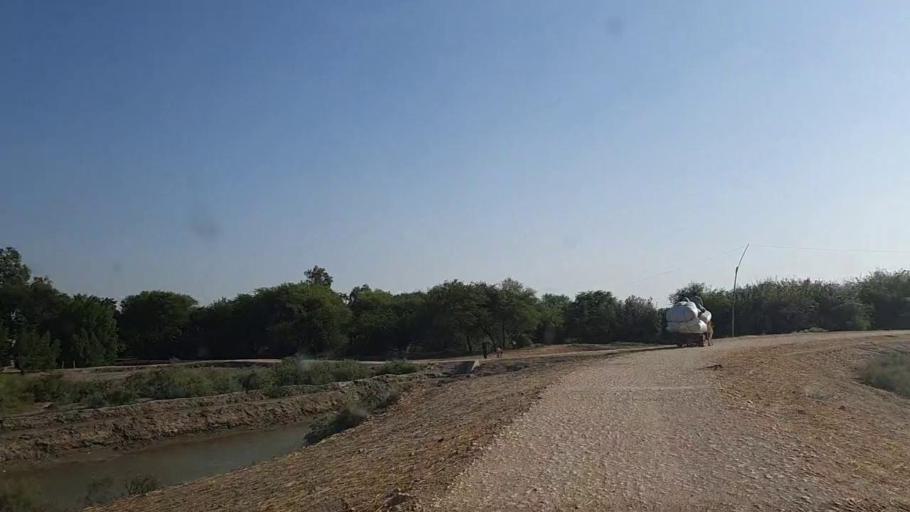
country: PK
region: Sindh
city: Daro Mehar
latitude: 24.6246
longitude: 68.0811
